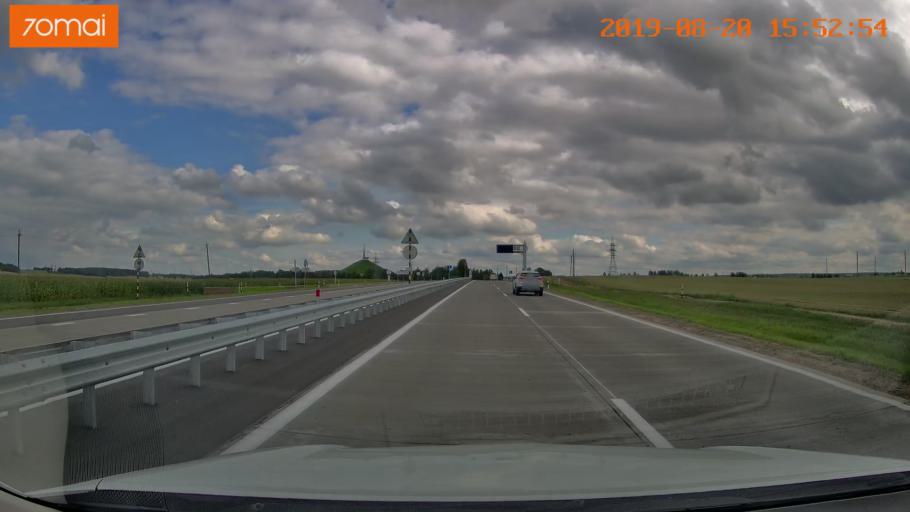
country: BY
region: Minsk
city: Slabada
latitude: 54.0243
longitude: 27.8822
